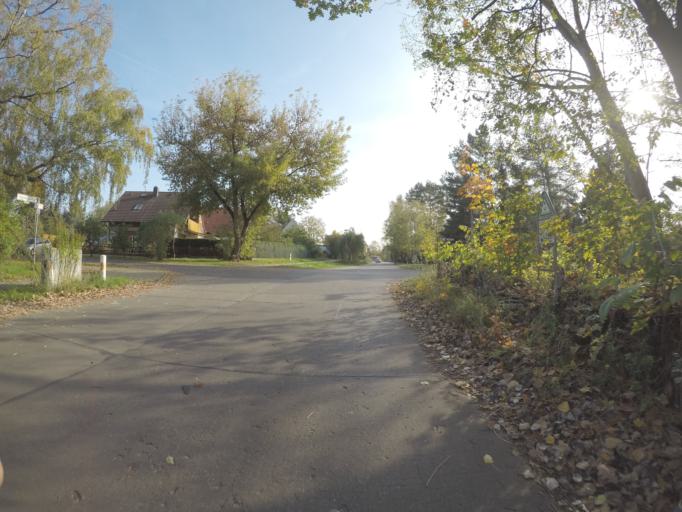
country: DE
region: Berlin
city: Altglienicke
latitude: 52.4145
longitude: 13.5430
